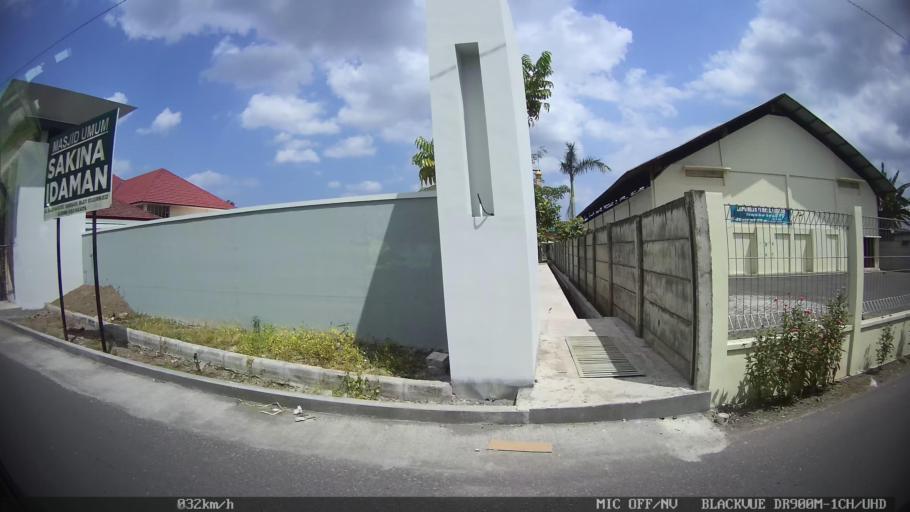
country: ID
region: Daerah Istimewa Yogyakarta
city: Yogyakarta
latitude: -7.7674
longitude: 110.3671
